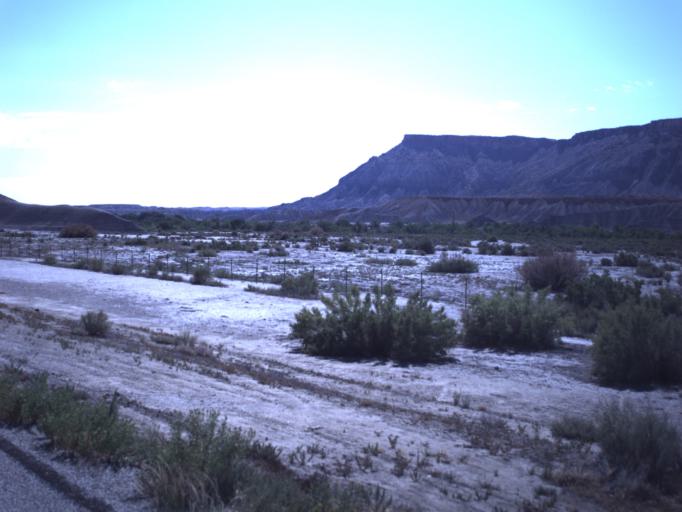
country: US
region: Utah
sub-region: Wayne County
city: Loa
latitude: 38.3428
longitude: -110.9917
